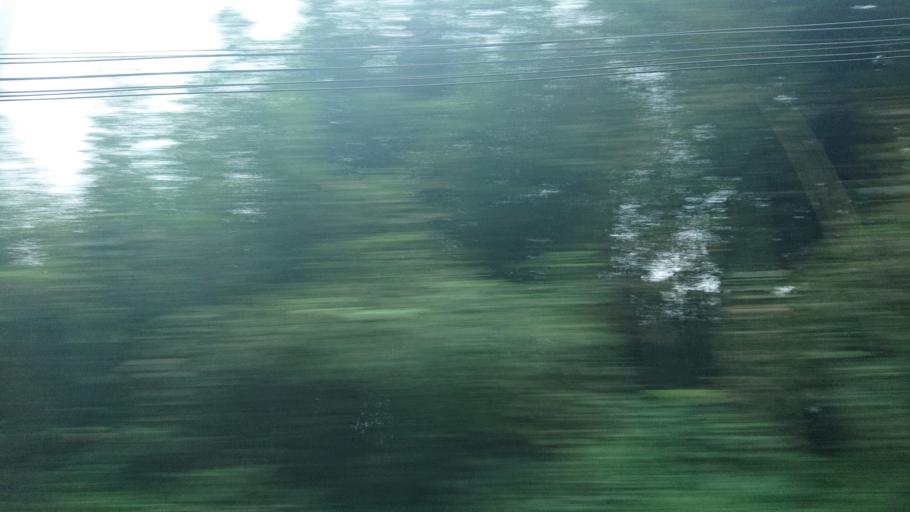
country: TW
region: Taiwan
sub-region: Chiayi
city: Jiayi Shi
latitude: 23.4760
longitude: 120.7192
